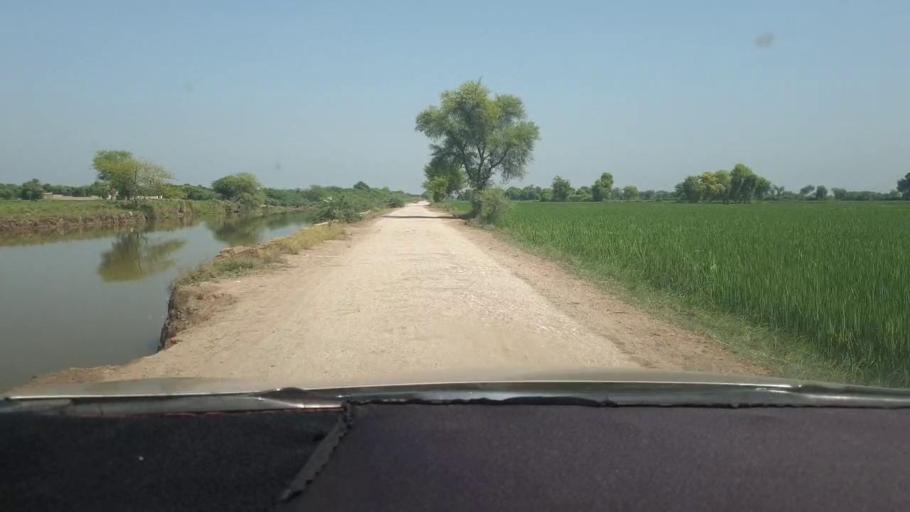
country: PK
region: Sindh
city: Miro Khan
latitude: 27.7045
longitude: 68.0792
